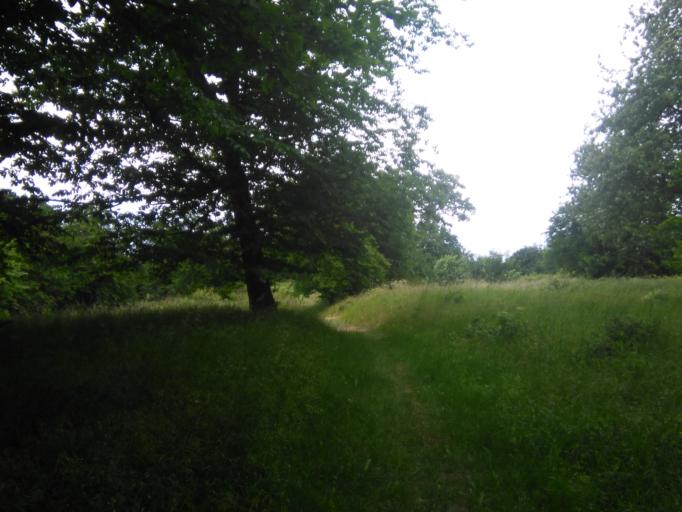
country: DK
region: Capital Region
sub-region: Bornholm Kommune
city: Akirkeby
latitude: 55.1149
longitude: 14.9068
